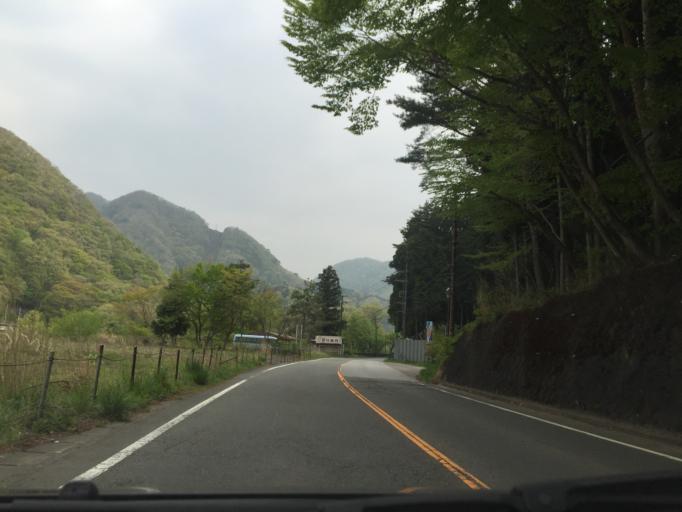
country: JP
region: Tochigi
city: Nikko
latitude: 36.8873
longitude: 139.7047
